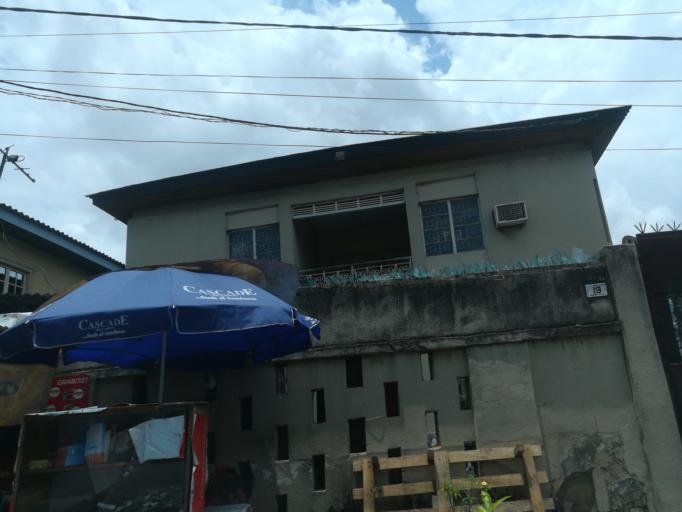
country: NG
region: Lagos
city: Somolu
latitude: 6.5494
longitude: 3.3592
